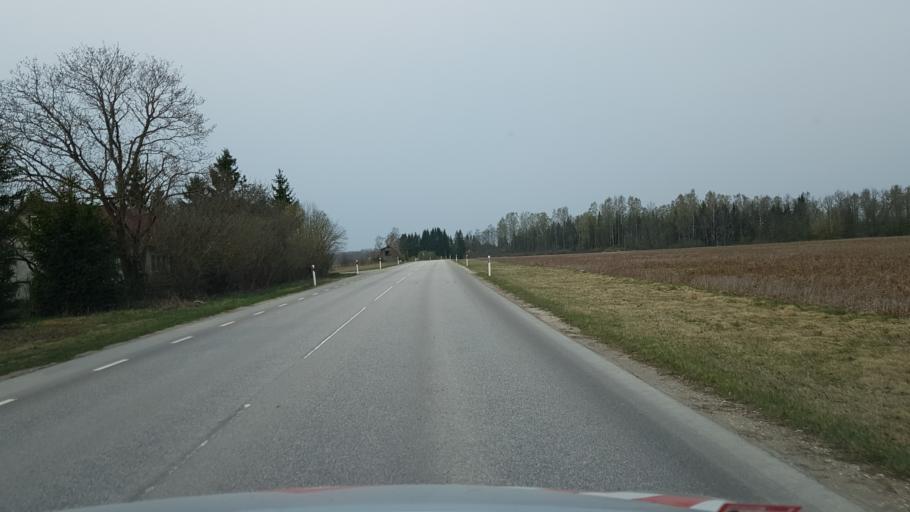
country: EE
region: Harju
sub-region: Raasiku vald
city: Arukula
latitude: 59.3800
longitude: 25.0074
